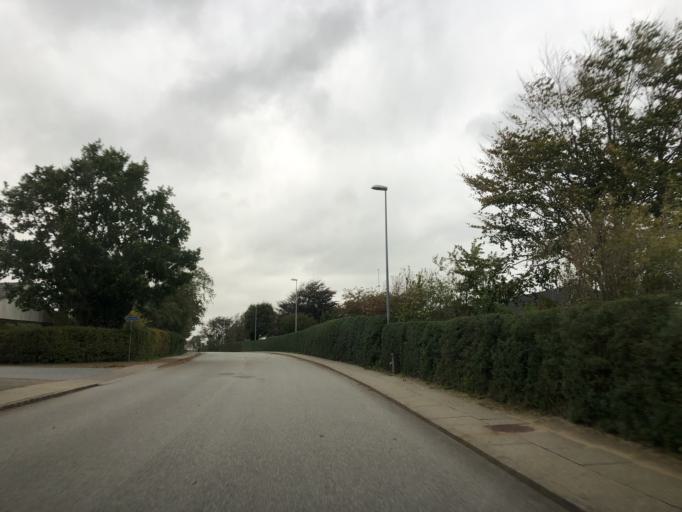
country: DK
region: Central Jutland
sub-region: Herning Kommune
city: Avlum
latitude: 56.2708
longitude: 8.7942
